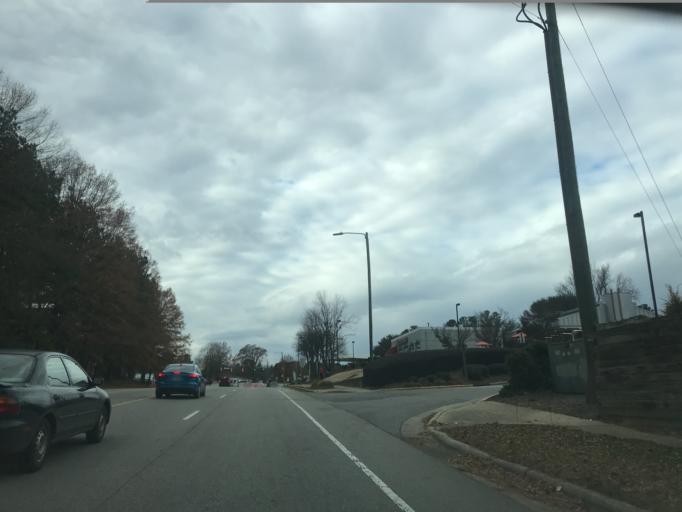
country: US
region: North Carolina
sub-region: Wake County
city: Raleigh
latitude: 35.8603
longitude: -78.5983
